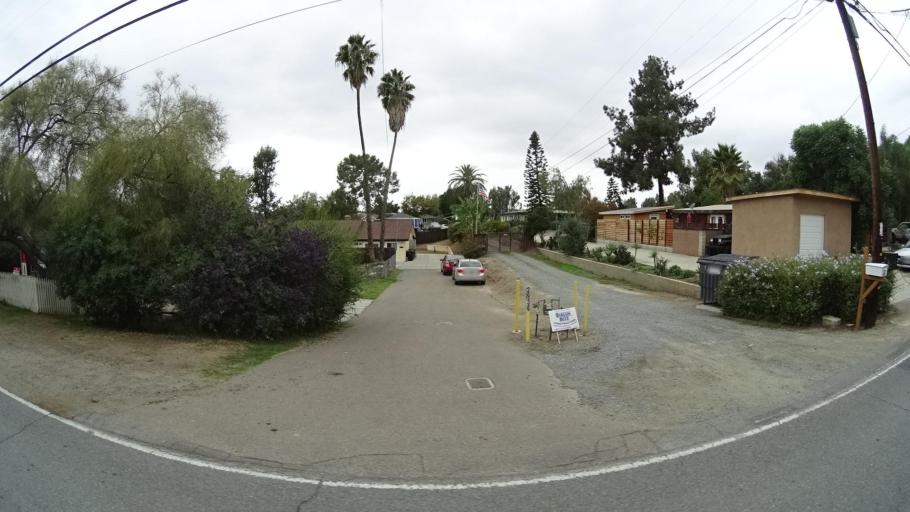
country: US
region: California
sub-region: San Diego County
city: Spring Valley
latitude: 32.7370
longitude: -117.0001
